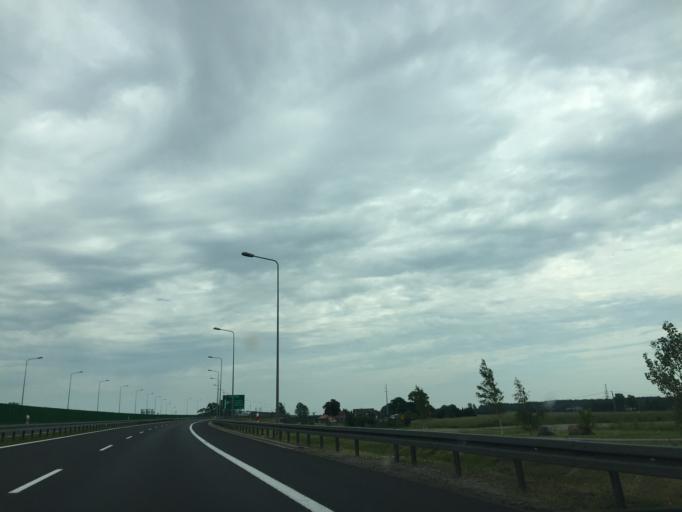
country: PL
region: Warmian-Masurian Voivodeship
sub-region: Powiat olsztynski
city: Biskupiec
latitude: 53.8485
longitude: 20.9589
